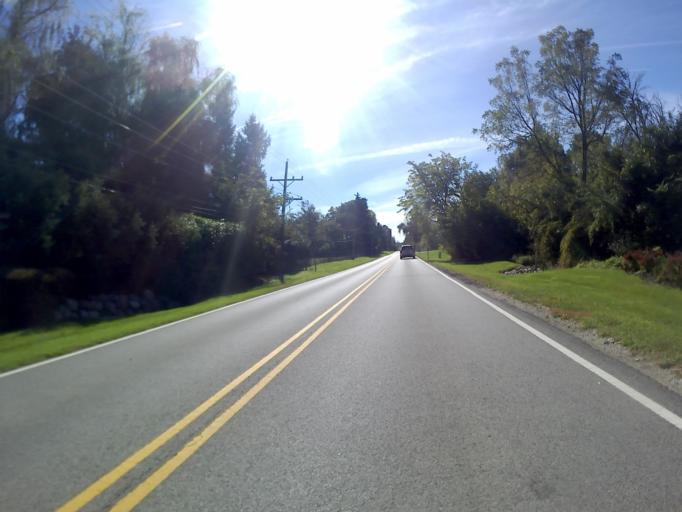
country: US
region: Illinois
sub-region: DuPage County
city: Lisle
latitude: 41.8217
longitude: -88.0974
